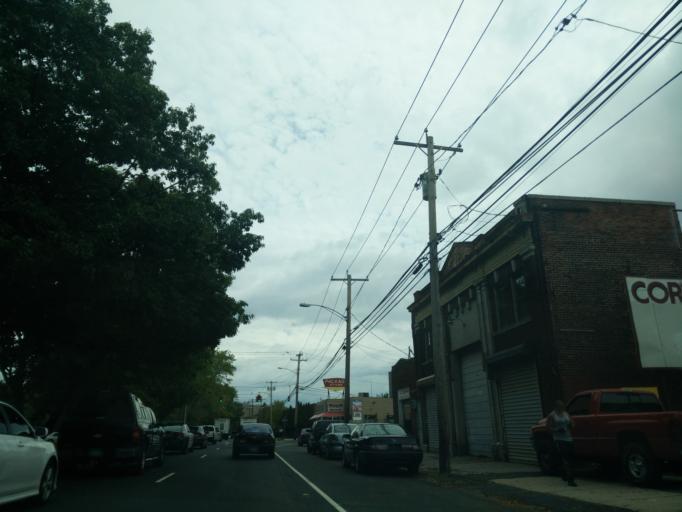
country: US
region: Connecticut
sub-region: Fairfield County
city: Bridgeport
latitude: 41.1960
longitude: -73.1773
